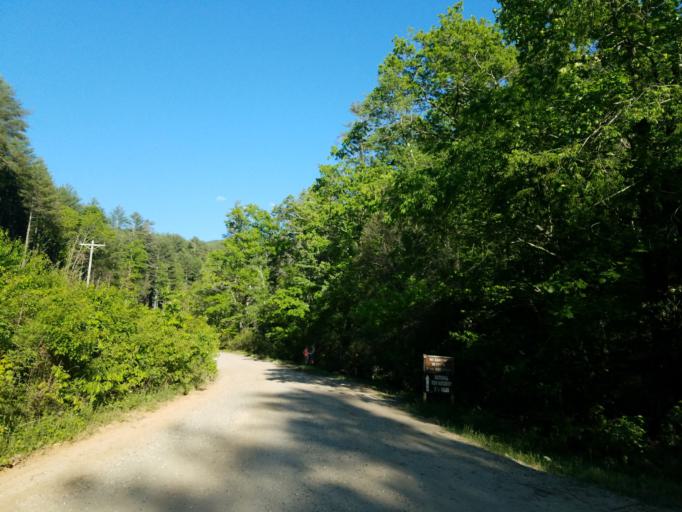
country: US
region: Georgia
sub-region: Fannin County
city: Blue Ridge
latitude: 34.7289
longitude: -84.1558
